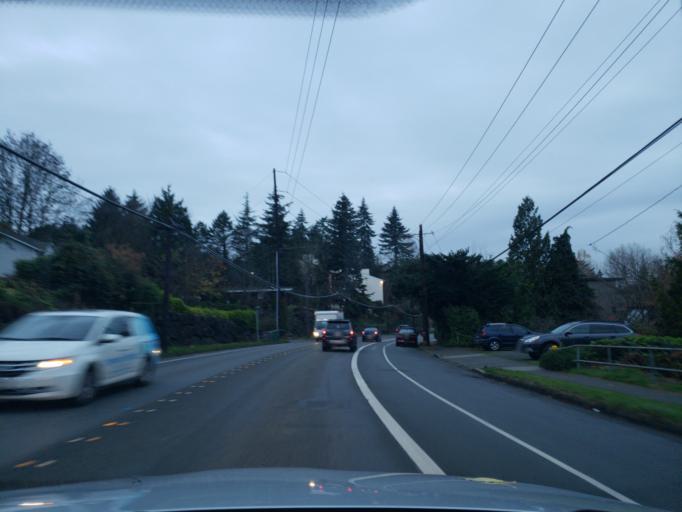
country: US
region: Washington
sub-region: Snohomish County
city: Lynnwood
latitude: 47.8066
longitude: -122.3089
